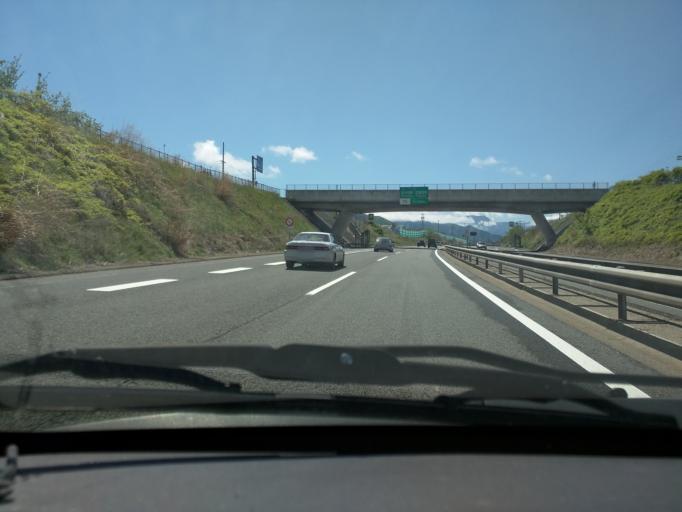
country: JP
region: Nagano
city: Nakano
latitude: 36.7381
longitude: 138.3174
